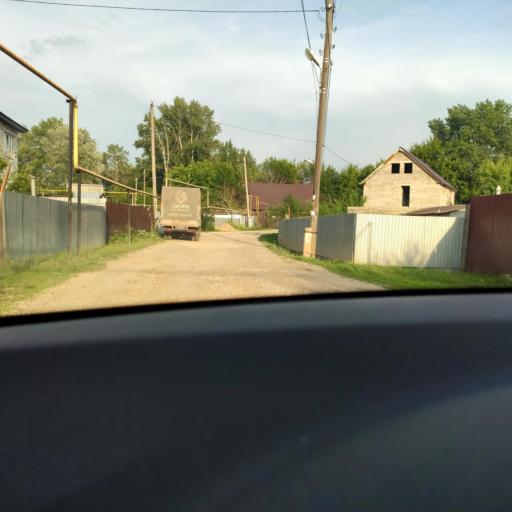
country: RU
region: Samara
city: Rozhdestveno
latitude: 53.1511
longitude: 50.0239
